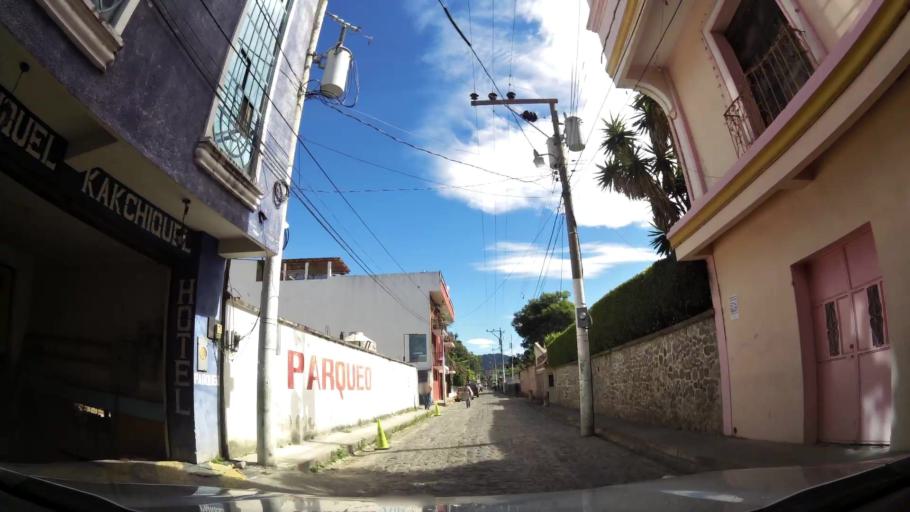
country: GT
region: Solola
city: Panajachel
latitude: 14.7401
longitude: -91.1597
